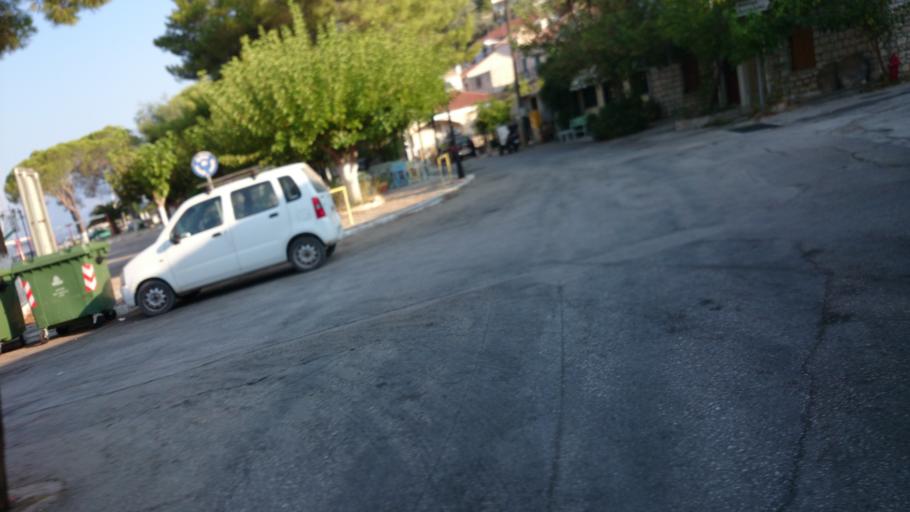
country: GR
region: Ionian Islands
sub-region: Lefkada
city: Nidri
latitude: 38.6631
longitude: 20.7860
